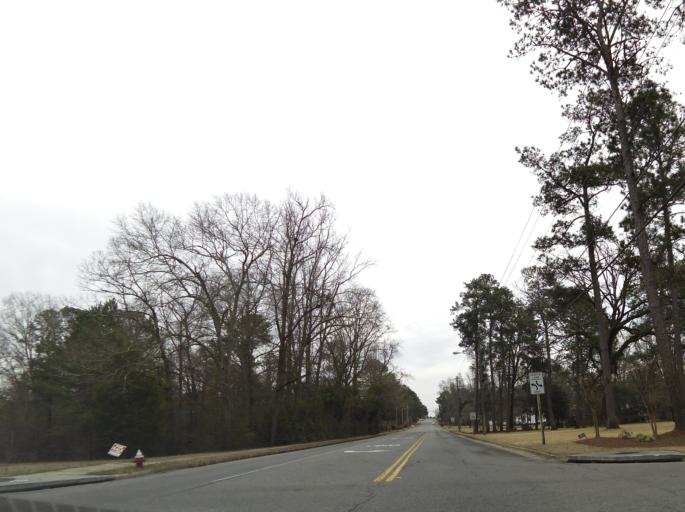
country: US
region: Georgia
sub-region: Bleckley County
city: Cochran
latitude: 32.3838
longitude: -83.3516
